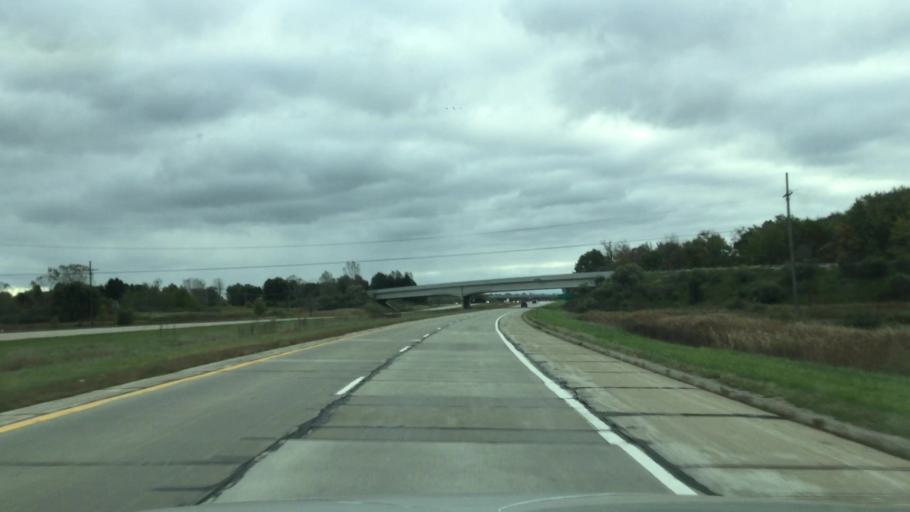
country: US
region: Michigan
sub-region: Saint Clair County
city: Capac
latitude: 42.9855
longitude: -82.8555
